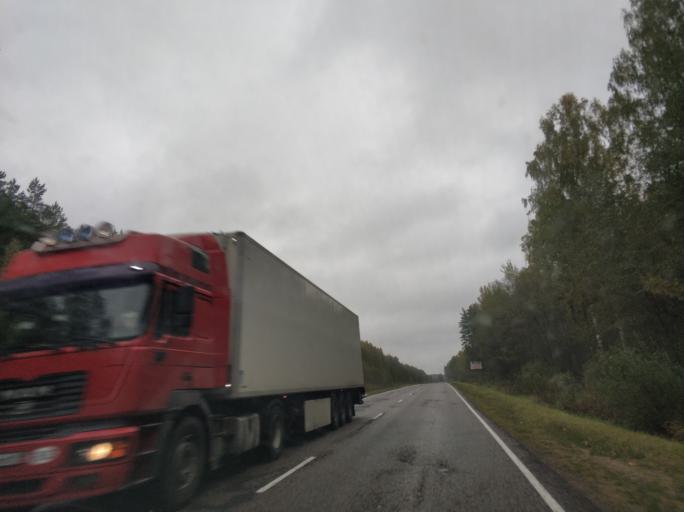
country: BY
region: Vitebsk
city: Rasony
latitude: 56.0874
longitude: 28.7192
